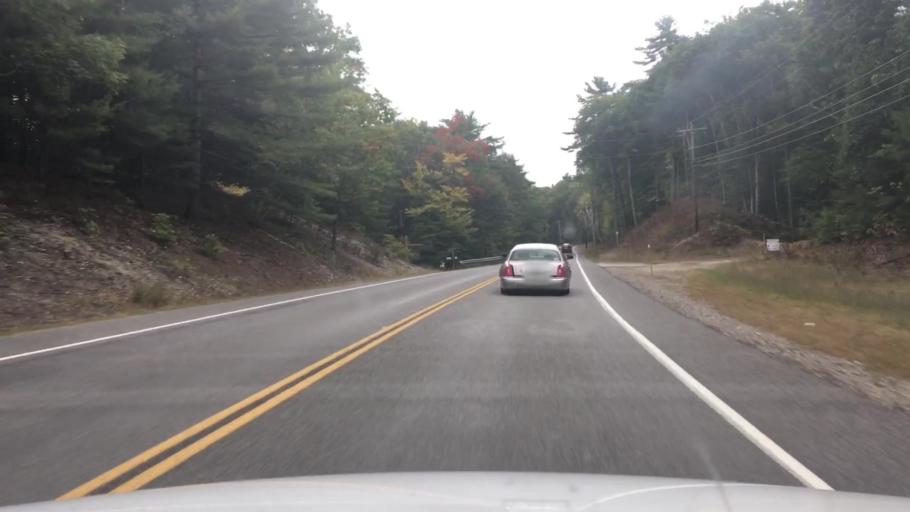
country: US
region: New Hampshire
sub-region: Strafford County
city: New Durham
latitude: 43.4925
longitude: -71.2551
